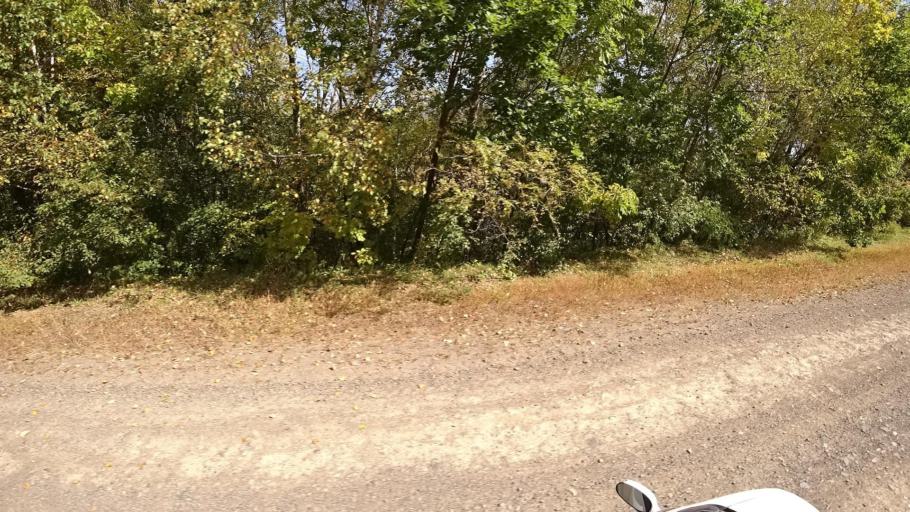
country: RU
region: Primorskiy
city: Yakovlevka
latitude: 44.7007
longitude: 133.6522
